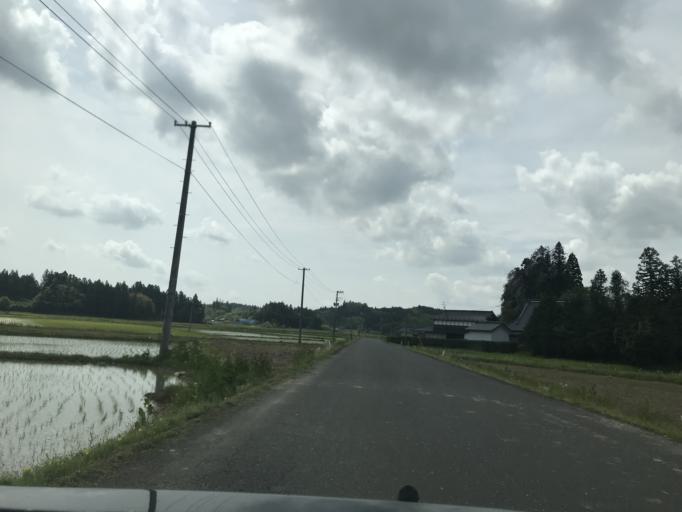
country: JP
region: Iwate
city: Ichinoseki
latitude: 38.8465
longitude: 141.0185
